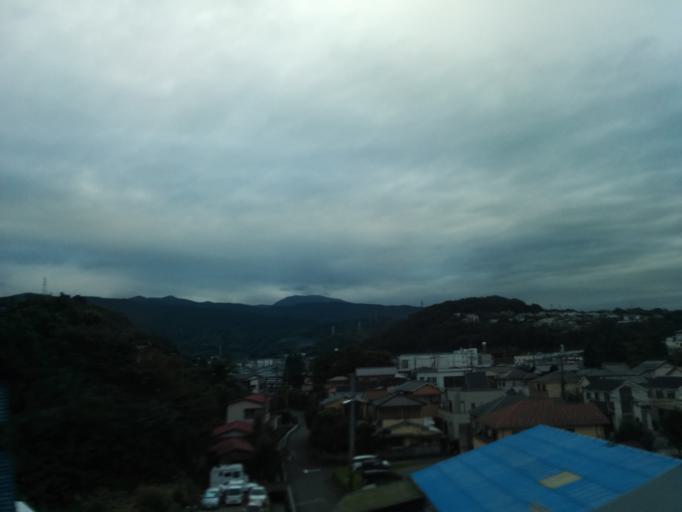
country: JP
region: Kanagawa
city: Odawara
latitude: 35.2417
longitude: 139.1439
